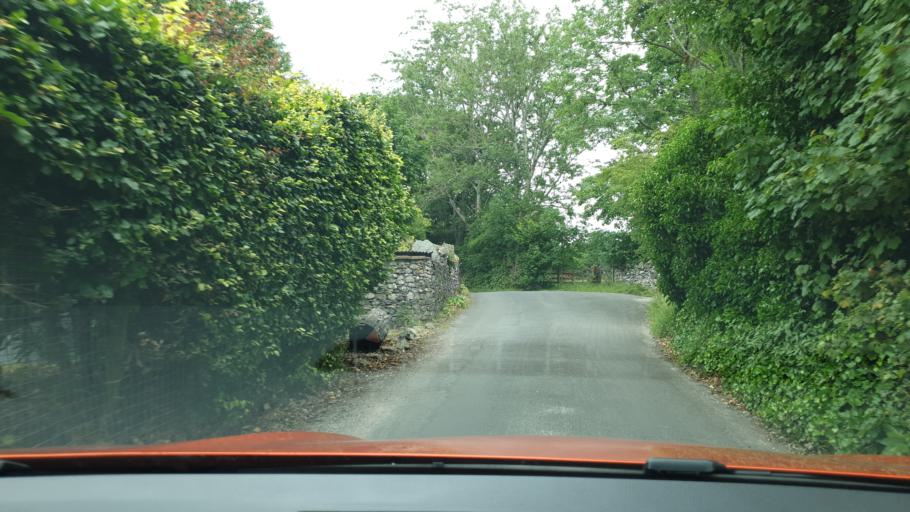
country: GB
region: England
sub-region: Cumbria
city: Penrith
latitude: 54.5815
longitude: -2.8524
